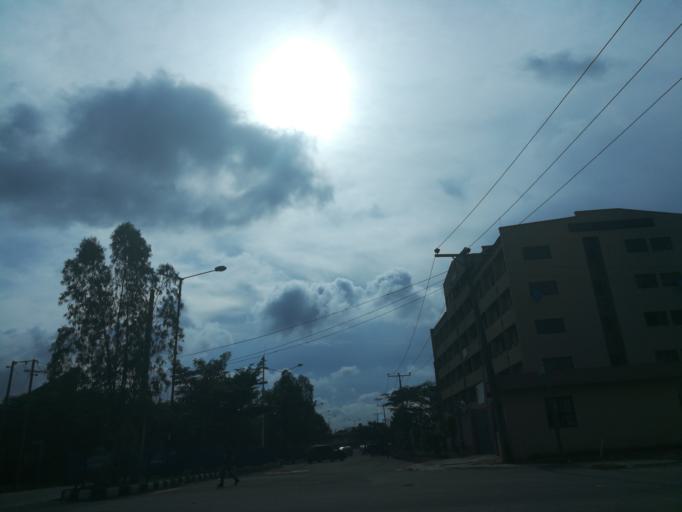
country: NG
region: Lagos
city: Ikeja
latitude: 6.6203
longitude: 3.3579
